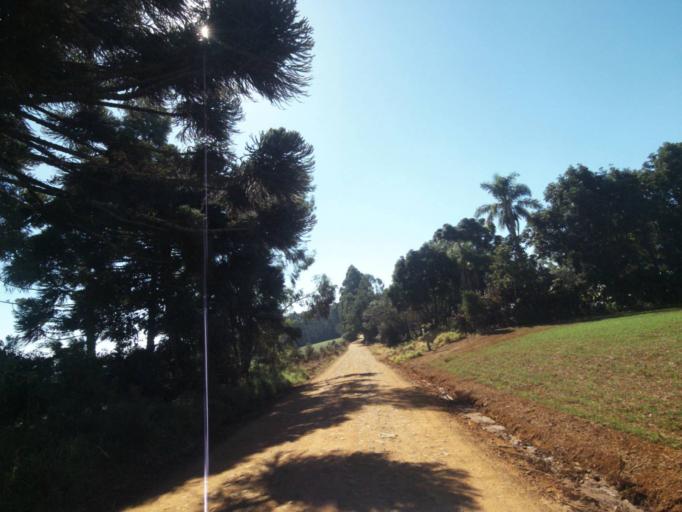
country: BR
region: Parana
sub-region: Tibagi
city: Tibagi
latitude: -24.5586
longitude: -50.6217
